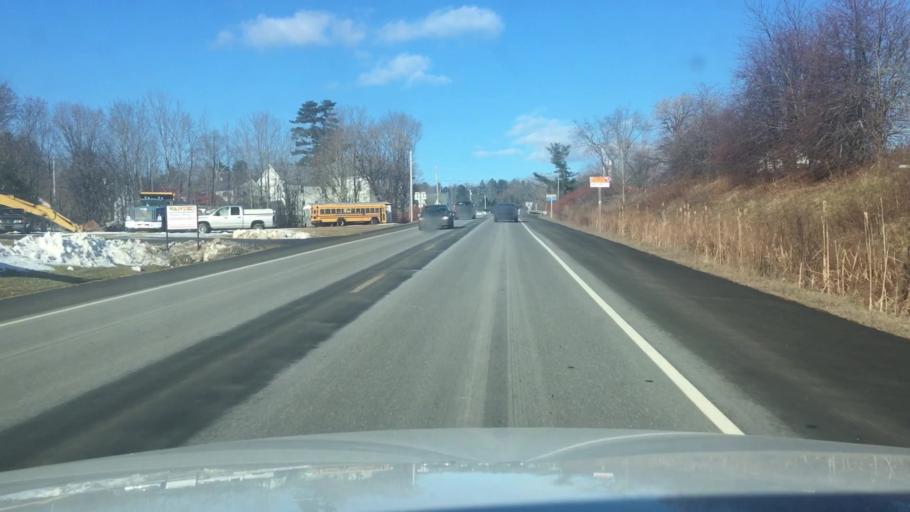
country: US
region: Maine
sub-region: Kennebec County
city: Waterville
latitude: 44.6049
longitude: -69.6607
